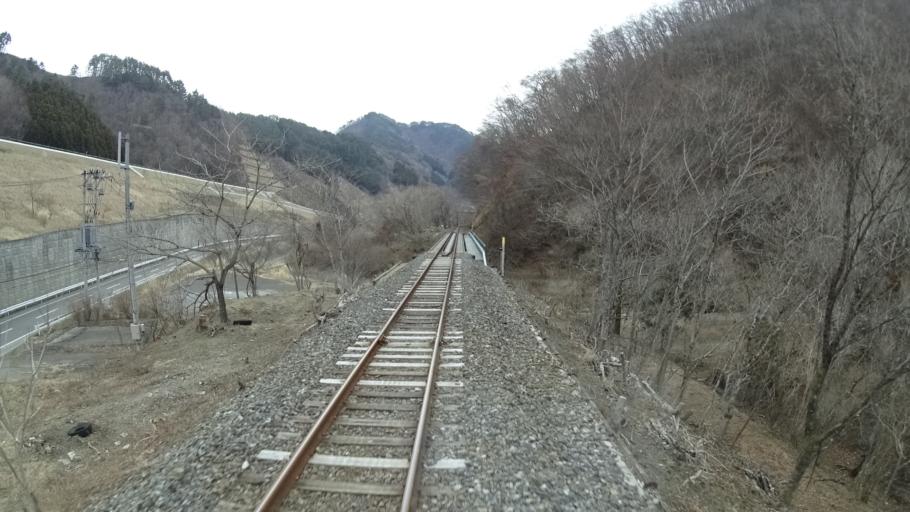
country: JP
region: Iwate
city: Kamaishi
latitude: 39.2968
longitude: 141.8682
